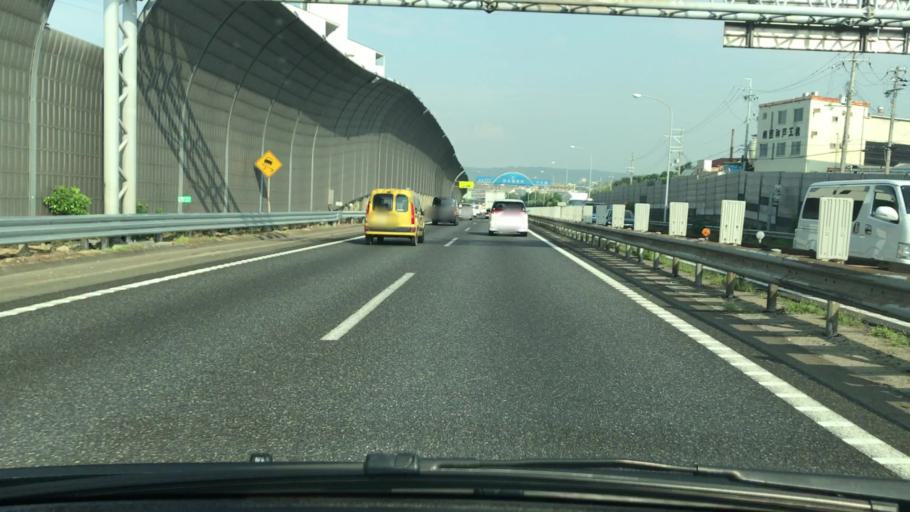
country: JP
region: Hyogo
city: Akashi
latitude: 34.6814
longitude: 134.9990
